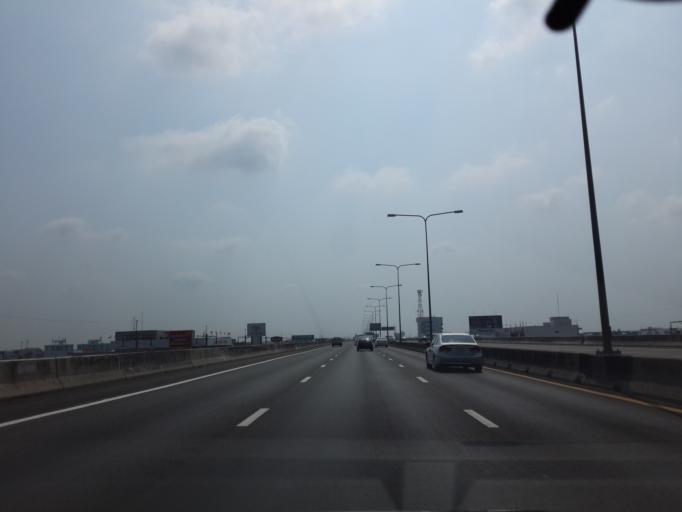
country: TH
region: Samut Prakan
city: Bang Bo District
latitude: 13.6166
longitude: 100.7473
